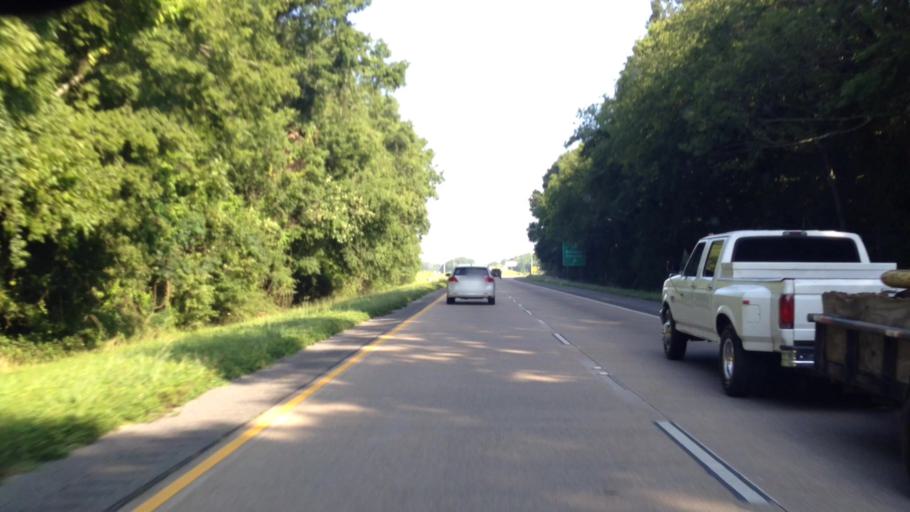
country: US
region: Louisiana
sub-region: Ascension Parish
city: Gonzales
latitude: 30.1891
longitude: -90.9129
